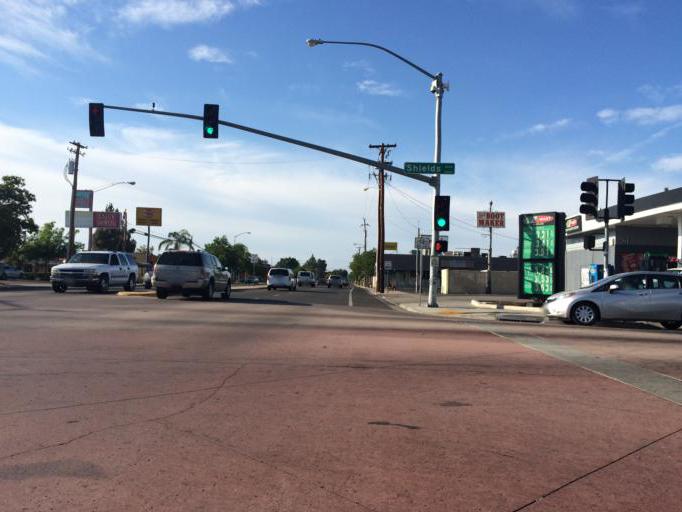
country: US
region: California
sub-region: Fresno County
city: Fresno
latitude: 36.7795
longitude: -119.7542
